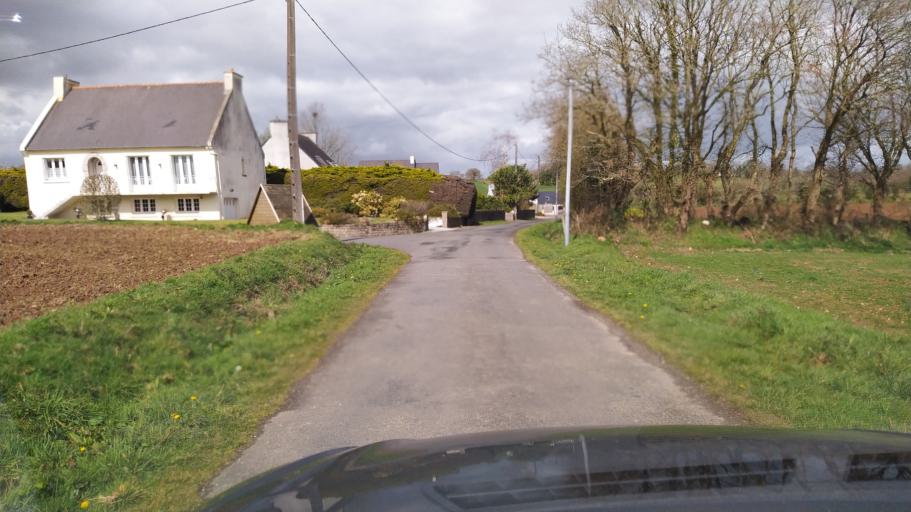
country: FR
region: Brittany
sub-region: Departement du Finistere
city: Bodilis
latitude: 48.5186
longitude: -4.1196
